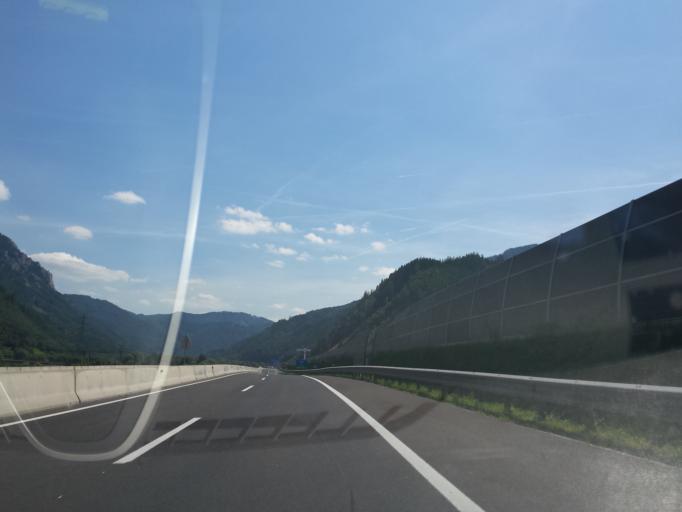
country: AT
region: Styria
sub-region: Politischer Bezirk Bruck-Muerzzuschlag
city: Pernegg an der Mur
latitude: 47.3475
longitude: 15.3462
